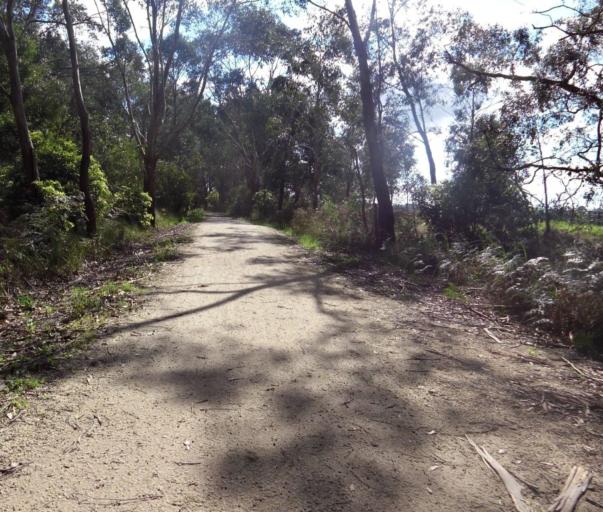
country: AU
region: Victoria
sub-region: Baw Baw
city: Warragul
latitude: -38.5762
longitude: 146.0285
